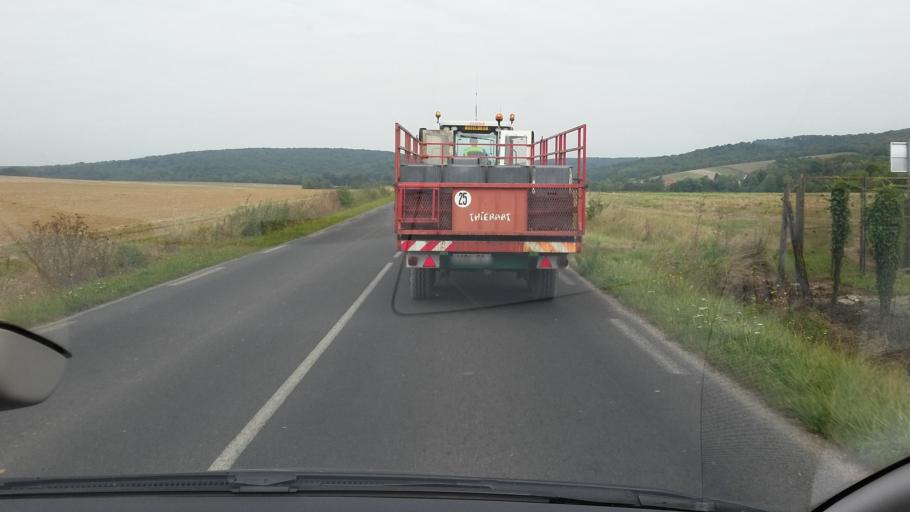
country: FR
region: Champagne-Ardenne
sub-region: Departement de la Marne
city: Tours-sur-Marne
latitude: 49.0937
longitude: 4.1043
